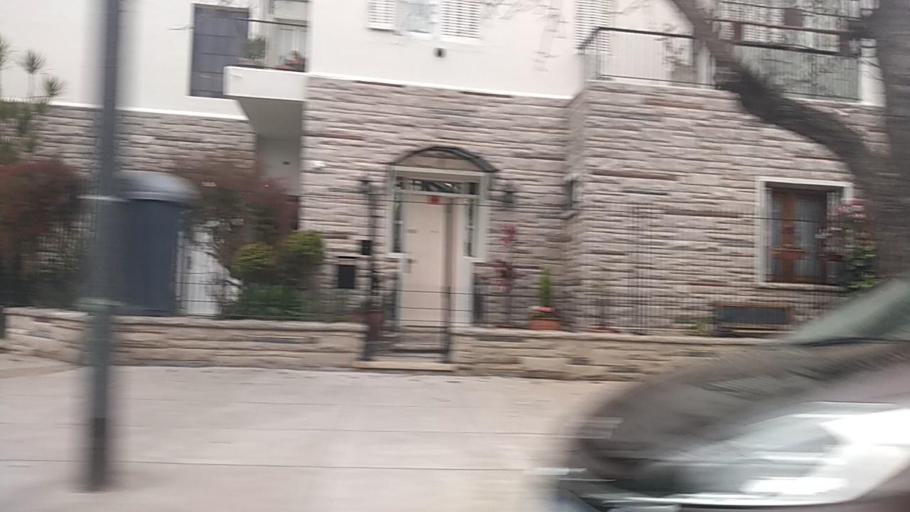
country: AR
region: Buenos Aires F.D.
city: Villa Santa Rita
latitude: -34.5979
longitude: -58.4941
